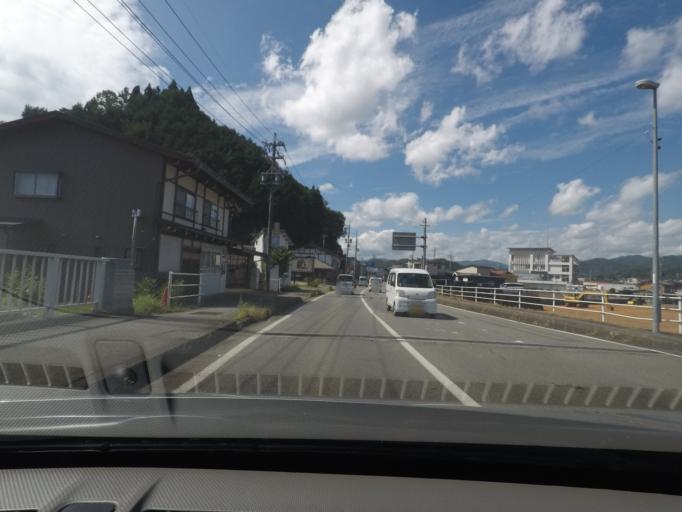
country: JP
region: Gifu
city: Takayama
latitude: 36.1540
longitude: 137.2594
